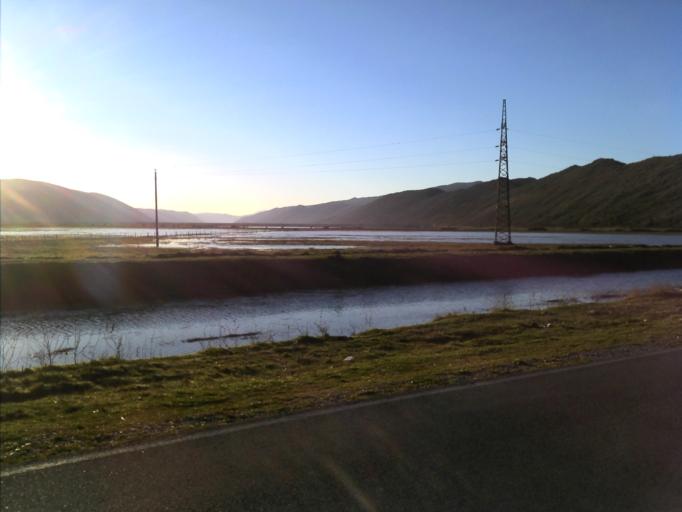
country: AL
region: Shkoder
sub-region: Rrethi i Shkodres
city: Dajc
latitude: 41.9344
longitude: 19.4430
